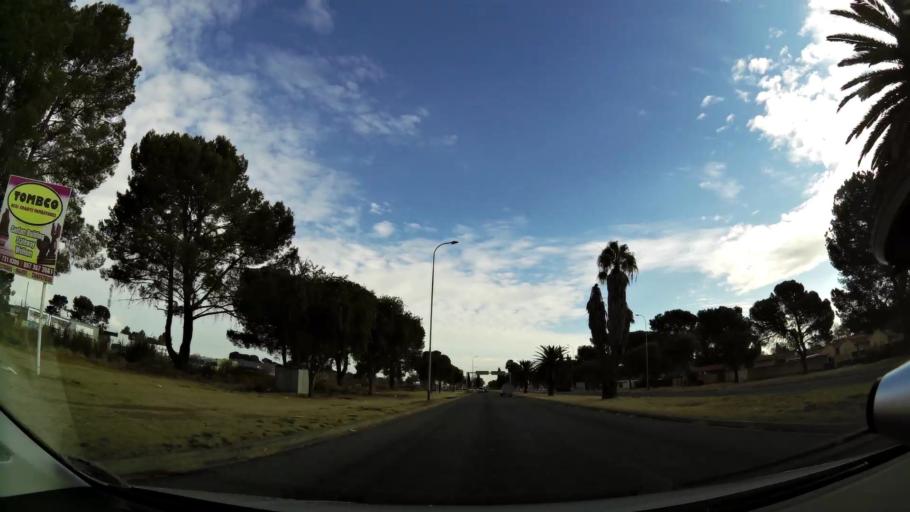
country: ZA
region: Orange Free State
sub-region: Lejweleputswa District Municipality
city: Welkom
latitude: -27.9853
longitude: 26.7584
